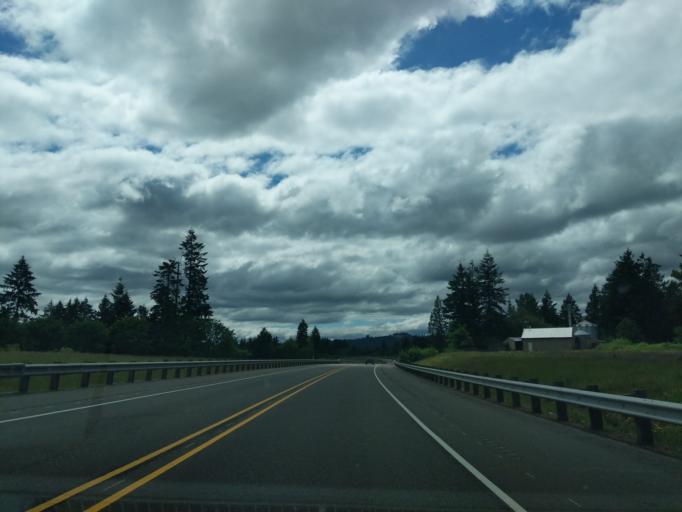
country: US
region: Oregon
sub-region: Yamhill County
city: Newberg
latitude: 45.2840
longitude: -122.9807
